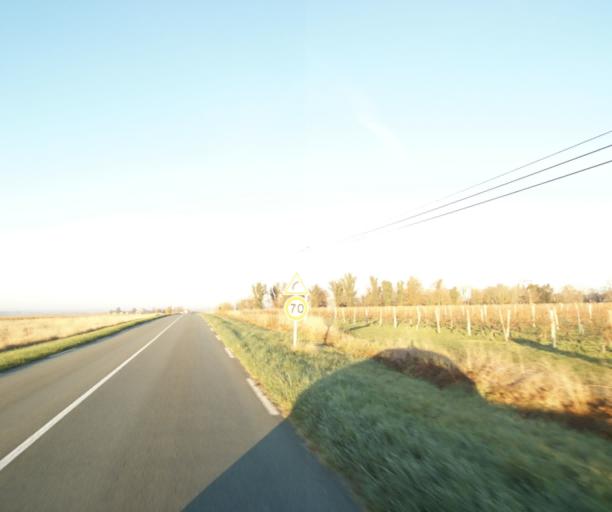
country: FR
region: Poitou-Charentes
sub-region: Departement de la Charente-Maritime
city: Cherac
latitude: 45.6996
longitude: -0.4599
